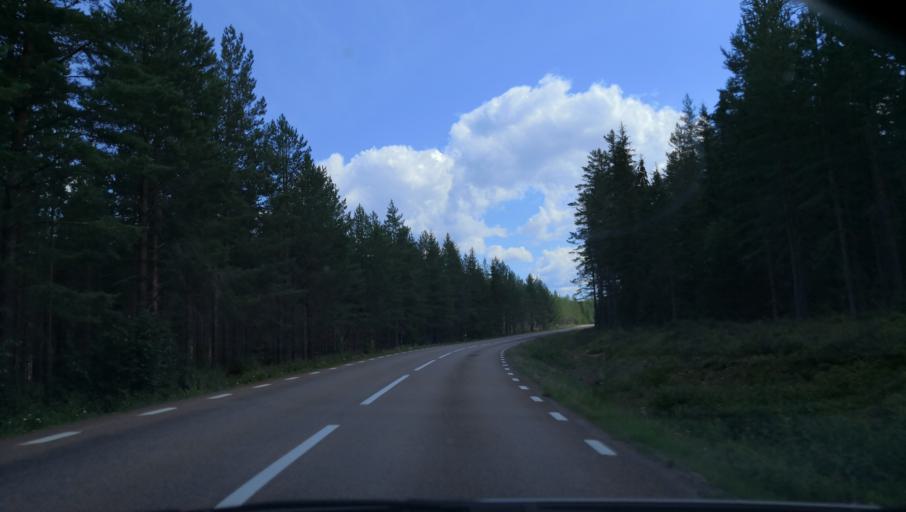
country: SE
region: Dalarna
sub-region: Rattviks Kommun
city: Vikarbyn
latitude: 61.1639
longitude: 15.0272
